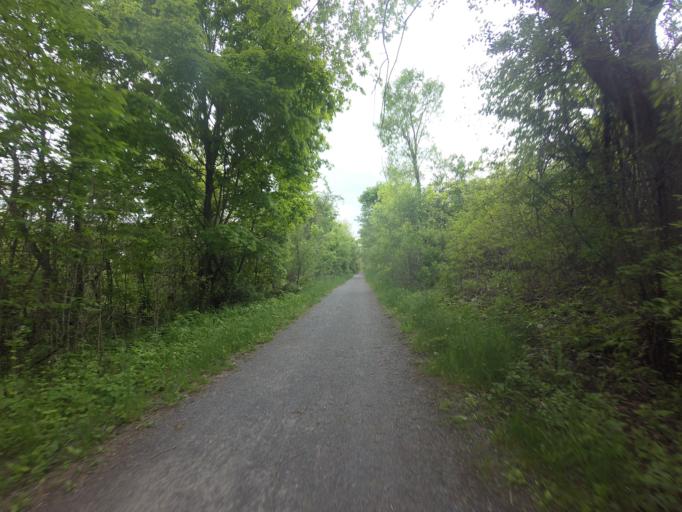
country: CA
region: Ontario
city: Kingston
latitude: 44.2992
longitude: -76.5726
